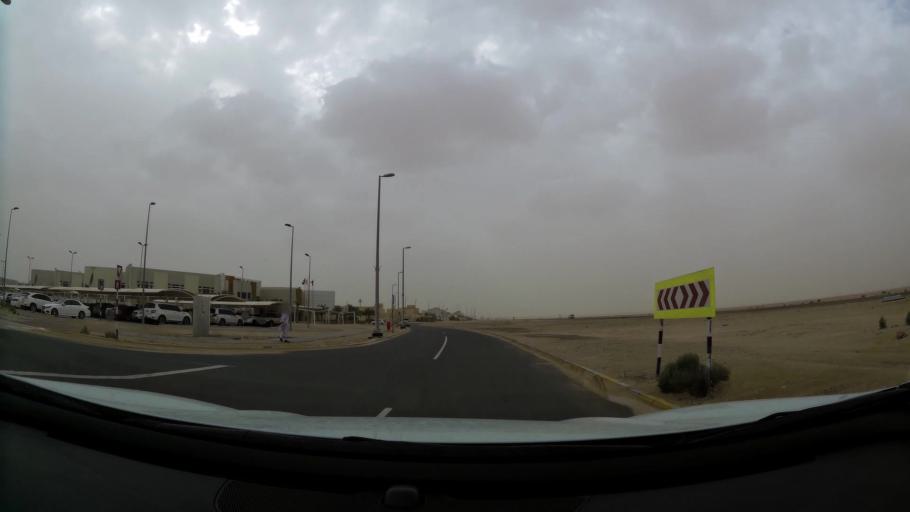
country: AE
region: Abu Dhabi
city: Abu Dhabi
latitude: 24.4477
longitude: 54.7099
